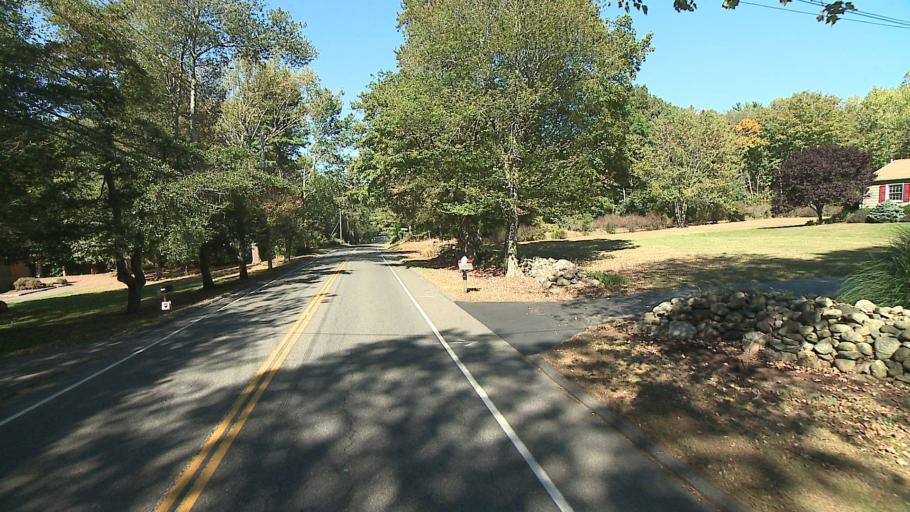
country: US
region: Connecticut
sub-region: New Haven County
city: Woodbridge
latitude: 41.3240
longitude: -73.0240
